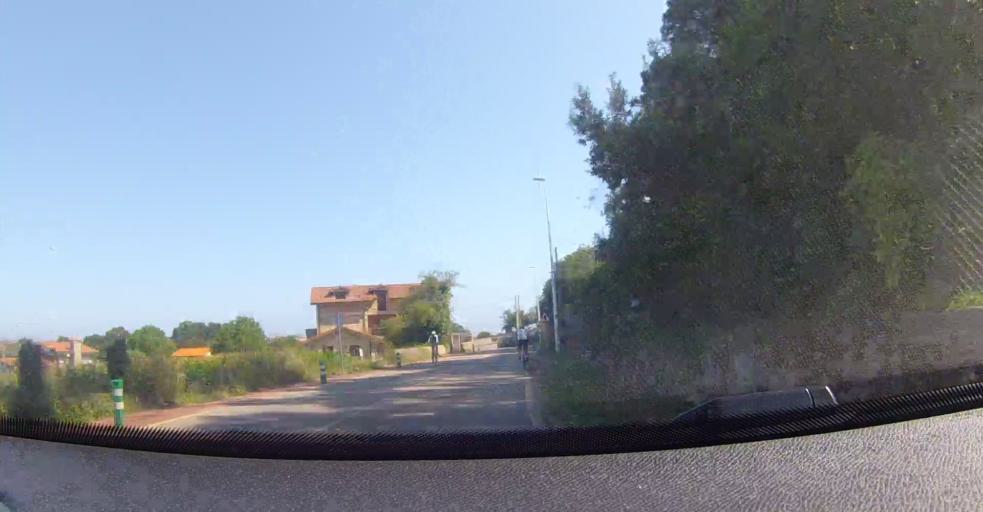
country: ES
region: Cantabria
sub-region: Provincia de Cantabria
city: Noja
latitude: 43.4648
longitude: -3.5197
